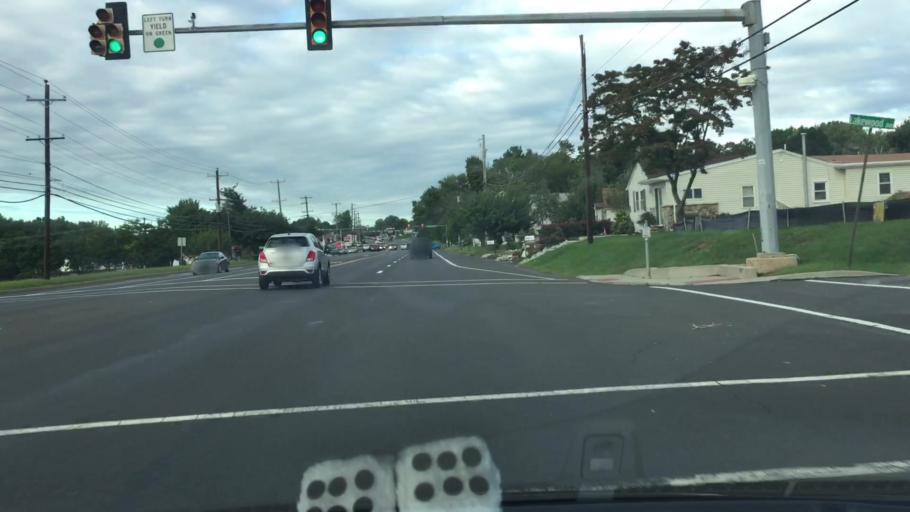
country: US
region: Pennsylvania
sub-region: Bucks County
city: Eddington
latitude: 40.0996
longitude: -74.9561
